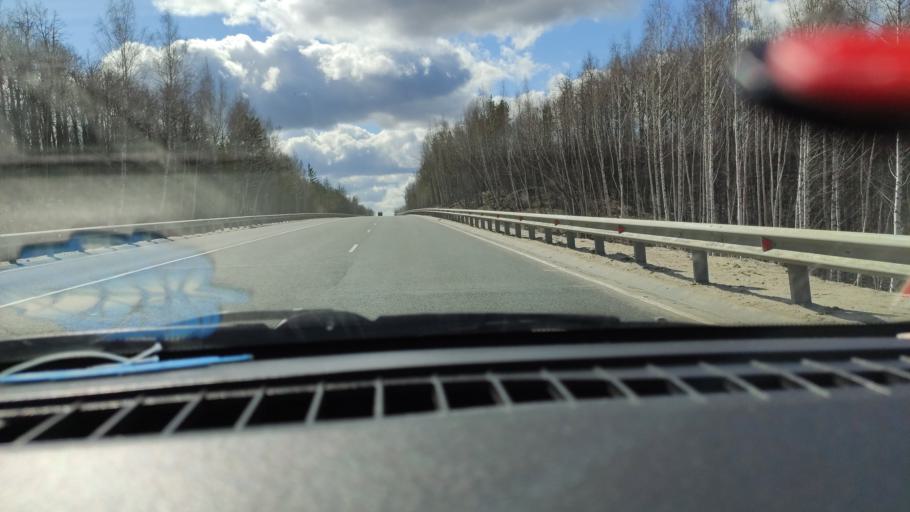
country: RU
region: Saratov
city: Khvalynsk
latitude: 52.4946
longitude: 48.0144
